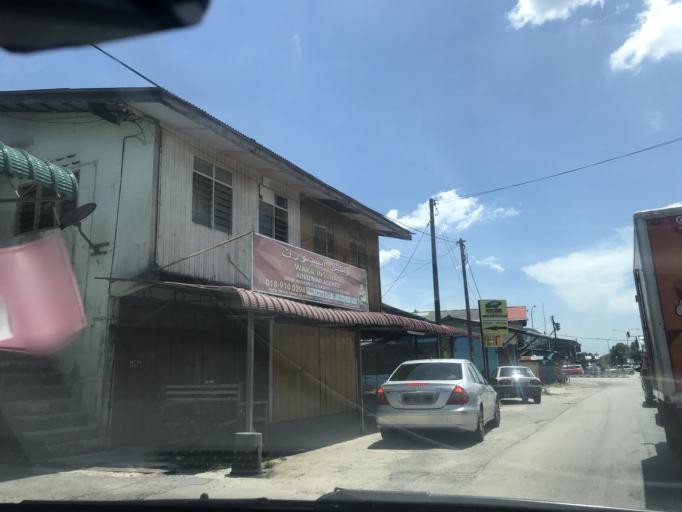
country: MY
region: Kelantan
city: Kota Bharu
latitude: 6.1234
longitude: 102.2718
